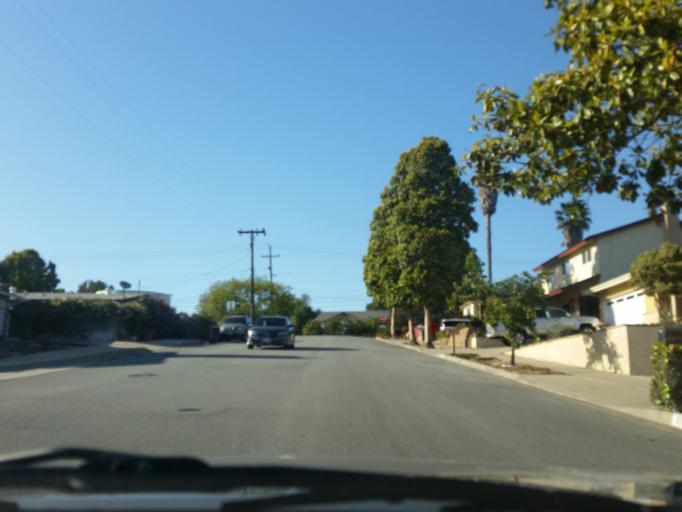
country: US
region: California
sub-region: San Luis Obispo County
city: Grover Beach
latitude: 35.1239
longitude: -120.6065
